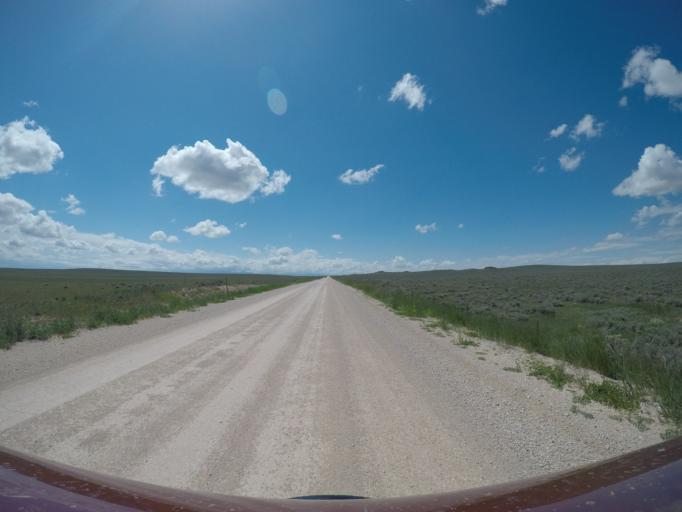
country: US
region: Wyoming
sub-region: Park County
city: Powell
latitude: 45.2051
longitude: -108.7449
